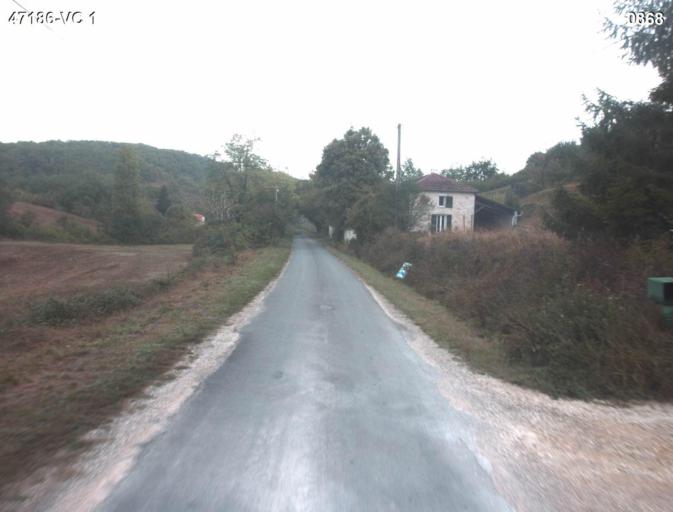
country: FR
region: Aquitaine
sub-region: Departement du Lot-et-Garonne
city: Port-Sainte-Marie
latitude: 44.1952
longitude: 0.4397
